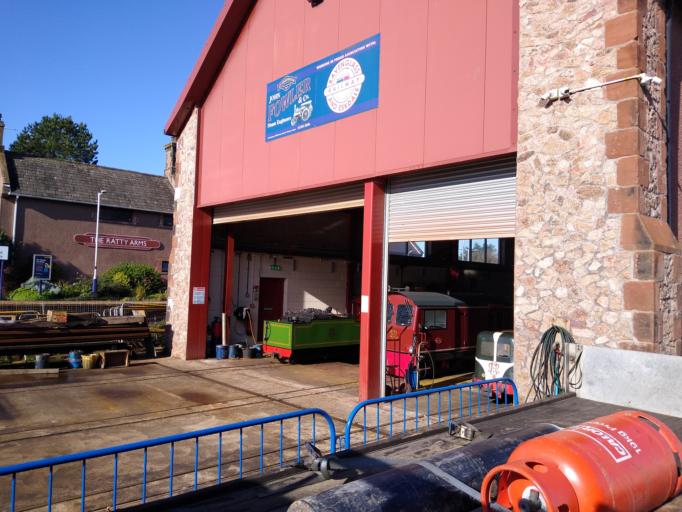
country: GB
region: England
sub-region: Cumbria
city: Seascale
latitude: 54.3557
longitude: -3.4085
